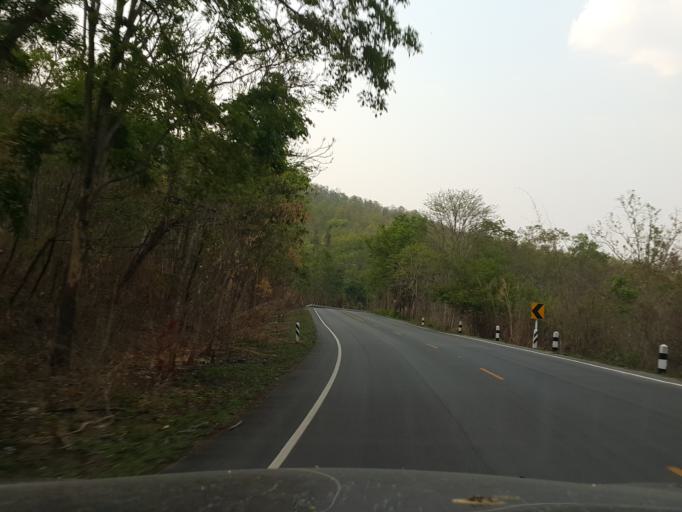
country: TH
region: Lamphun
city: Li
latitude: 17.8440
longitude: 99.0174
